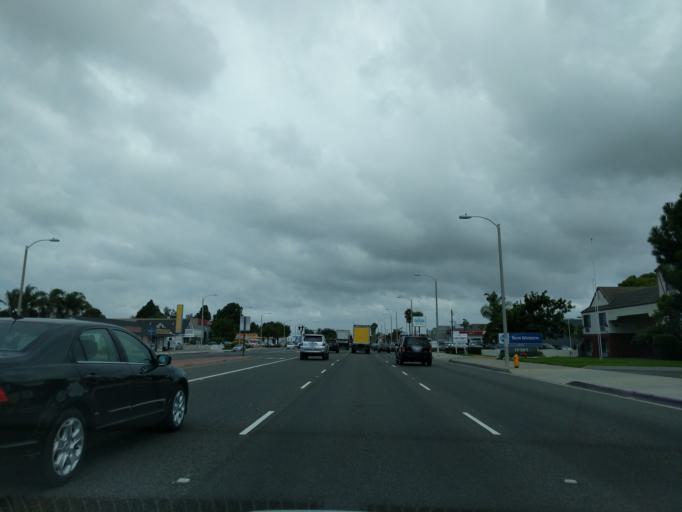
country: US
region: California
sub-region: Orange County
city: Huntington Beach
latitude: 33.6807
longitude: -117.9886
